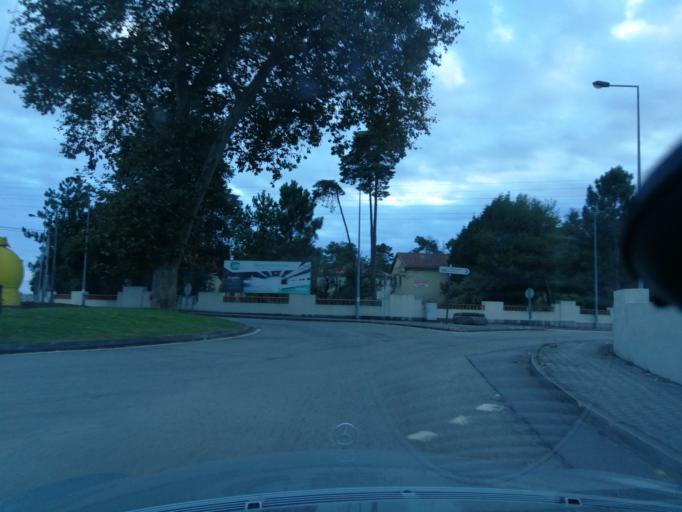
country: PT
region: Aveiro
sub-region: Estarreja
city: Beduido
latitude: 40.7754
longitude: -8.5682
